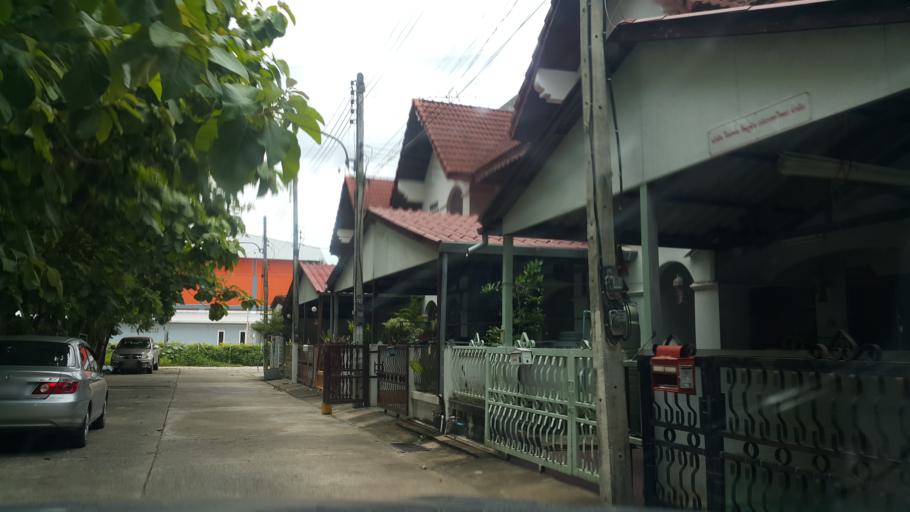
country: TH
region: Chiang Mai
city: Chiang Mai
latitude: 18.7672
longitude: 99.0106
